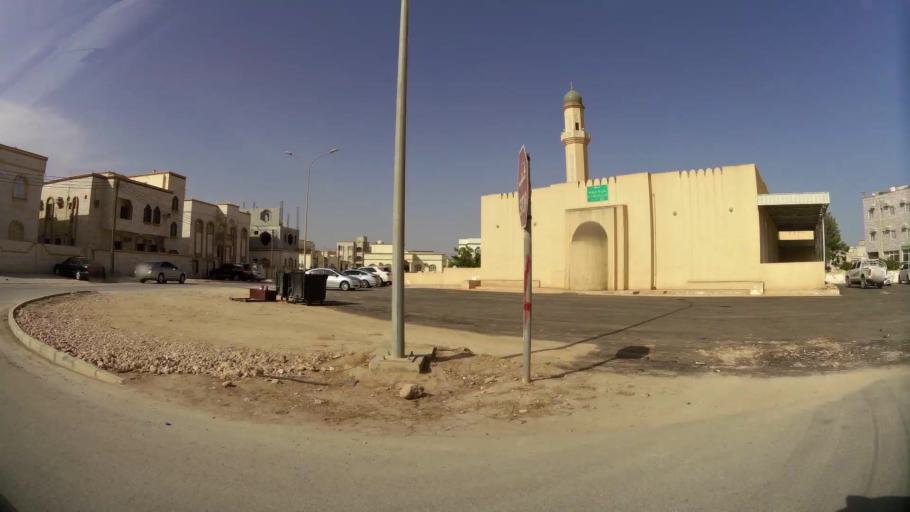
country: OM
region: Zufar
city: Salalah
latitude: 17.0104
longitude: 54.0145
